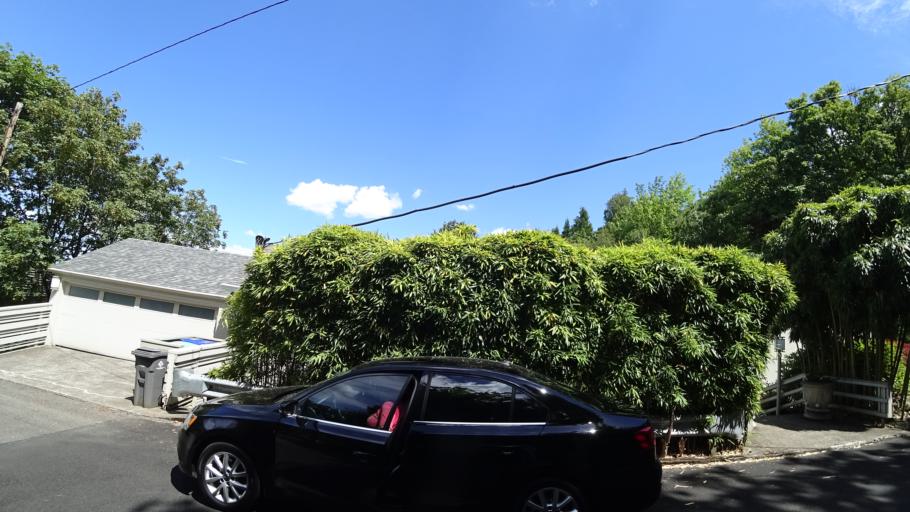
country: US
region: Oregon
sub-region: Multnomah County
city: Portland
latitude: 45.5081
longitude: -122.6906
